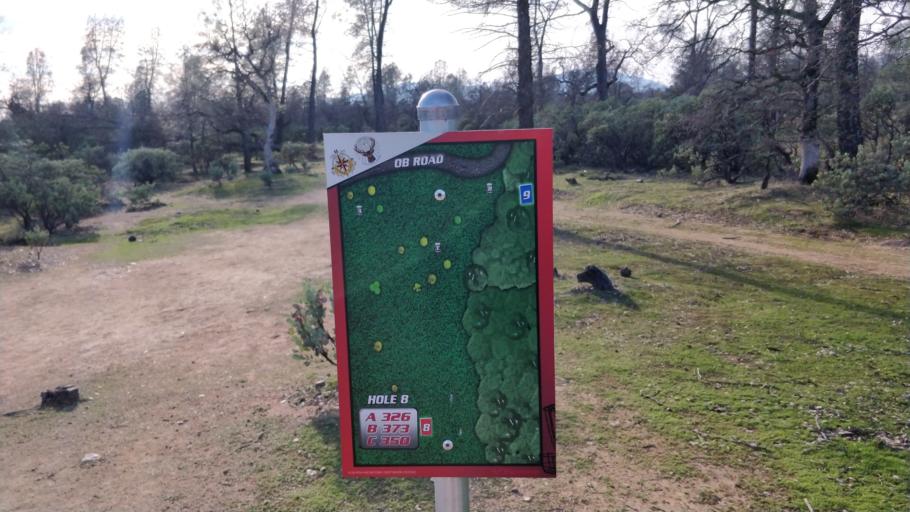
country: US
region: California
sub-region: Shasta County
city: Redding
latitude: 40.6326
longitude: -122.3987
